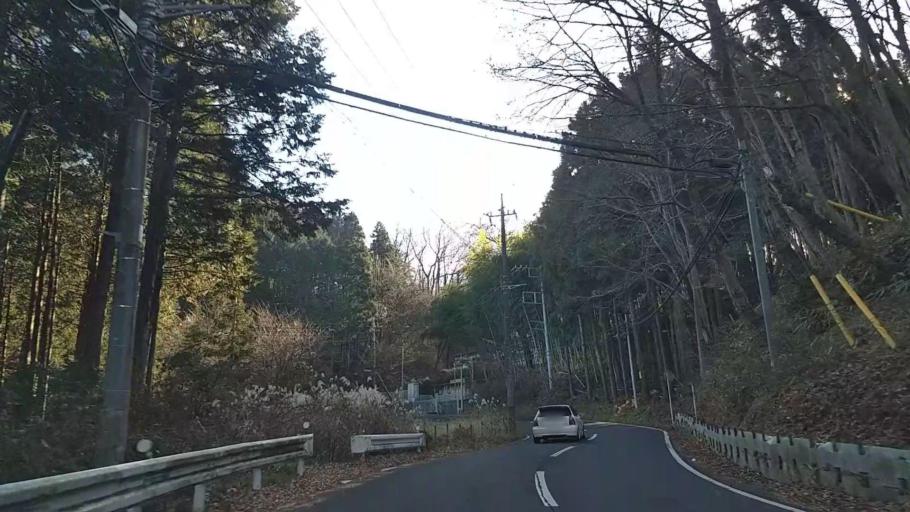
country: JP
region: Yamanashi
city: Uenohara
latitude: 35.5449
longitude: 139.1317
